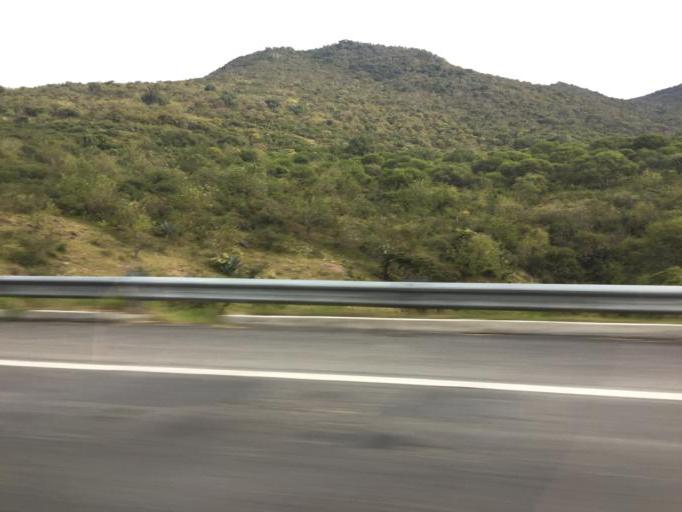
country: MX
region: Michoacan
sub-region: Cuitzeo
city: San Juan Benito Juarez (San Juan Tararameo)
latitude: 19.9042
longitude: -101.1335
